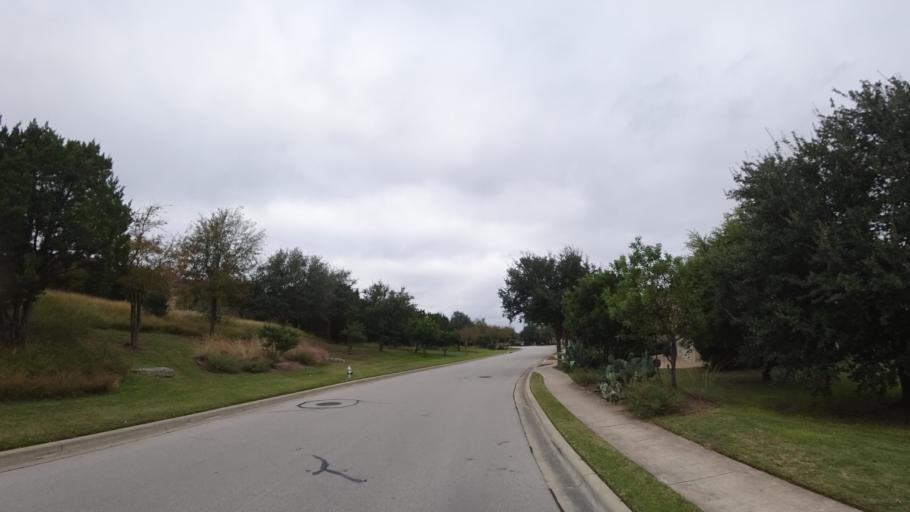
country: US
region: Texas
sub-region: Travis County
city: Hudson Bend
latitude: 30.3601
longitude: -97.9050
